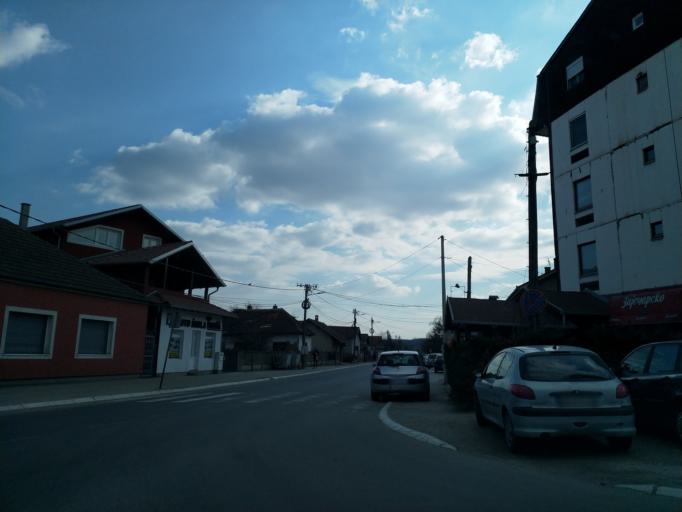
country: RS
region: Central Serbia
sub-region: Sumadijski Okrug
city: Batocina
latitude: 44.1505
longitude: 21.0776
